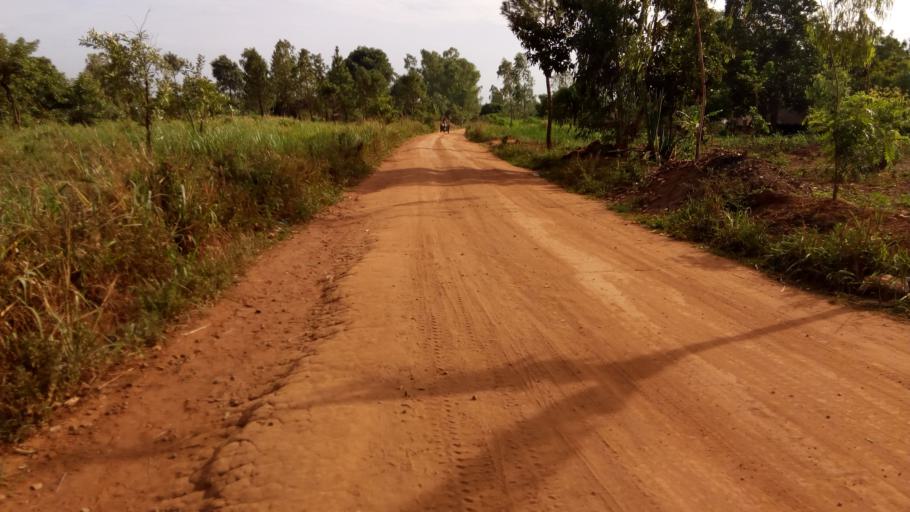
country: UG
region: Northern Region
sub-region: Gulu District
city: Gulu
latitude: 2.7894
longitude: 32.3226
